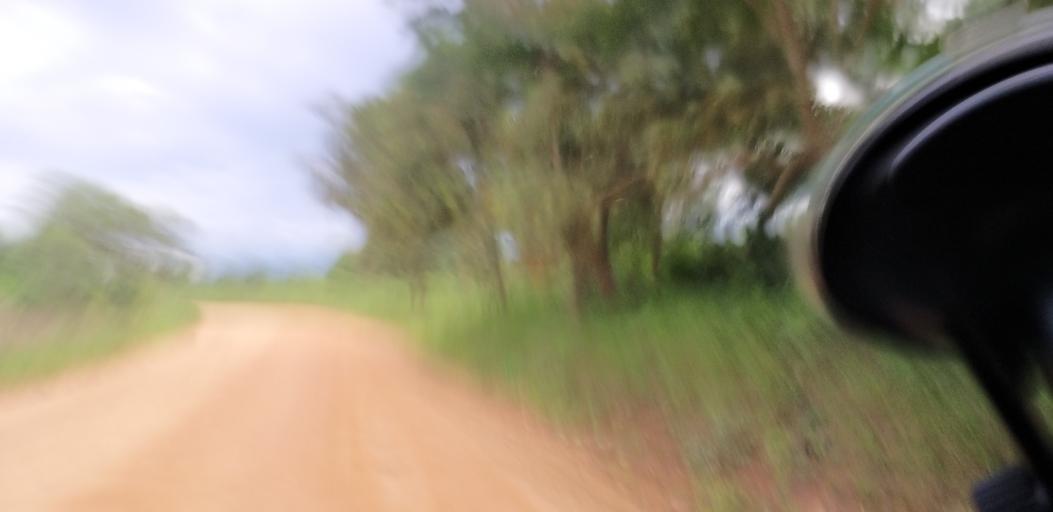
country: ZM
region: Lusaka
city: Chongwe
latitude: -15.1803
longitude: 28.4511
